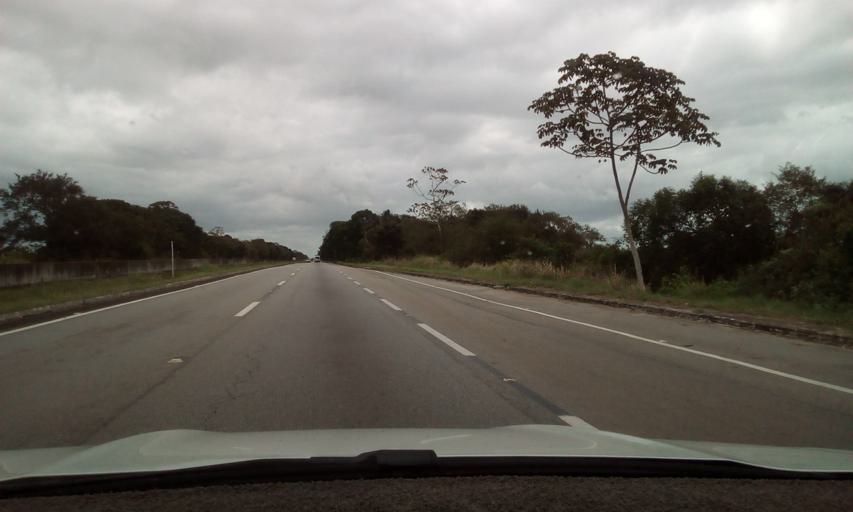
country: BR
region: Paraiba
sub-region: Mamanguape
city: Mamanguape
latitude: -6.9040
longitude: -35.1187
